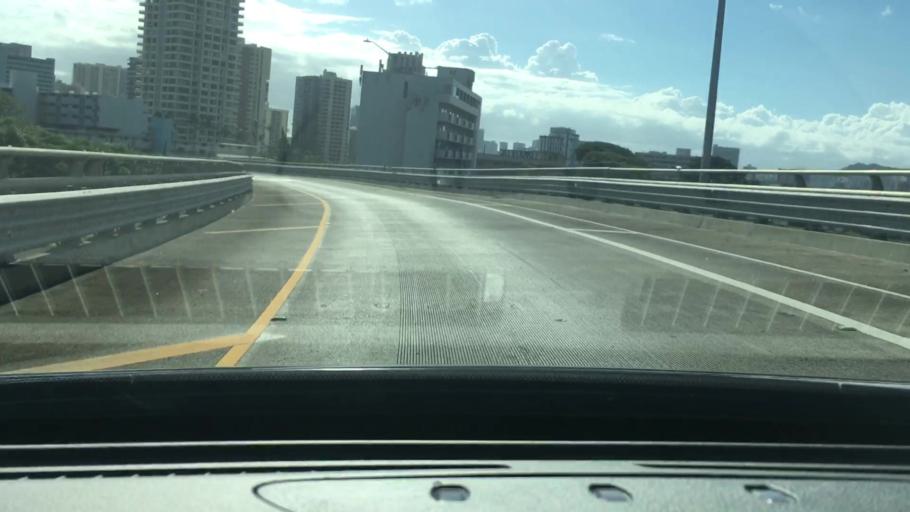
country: US
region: Hawaii
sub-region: Honolulu County
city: Honolulu
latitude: 21.2896
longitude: -157.8153
